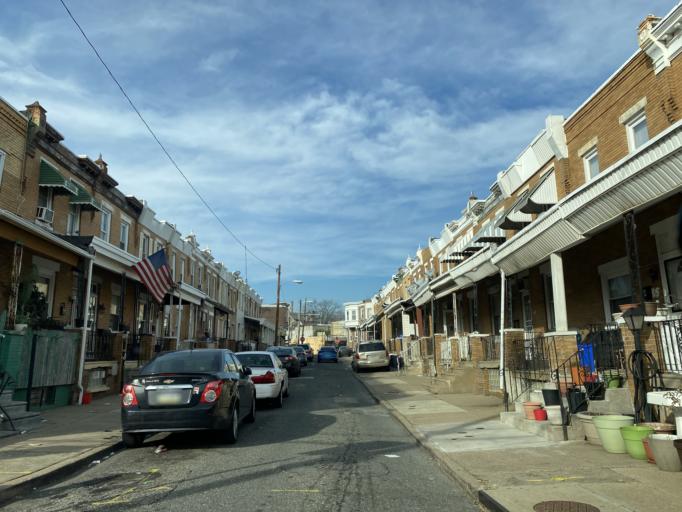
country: US
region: New Jersey
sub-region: Burlington County
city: Palmyra
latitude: 40.0077
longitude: -75.0858
